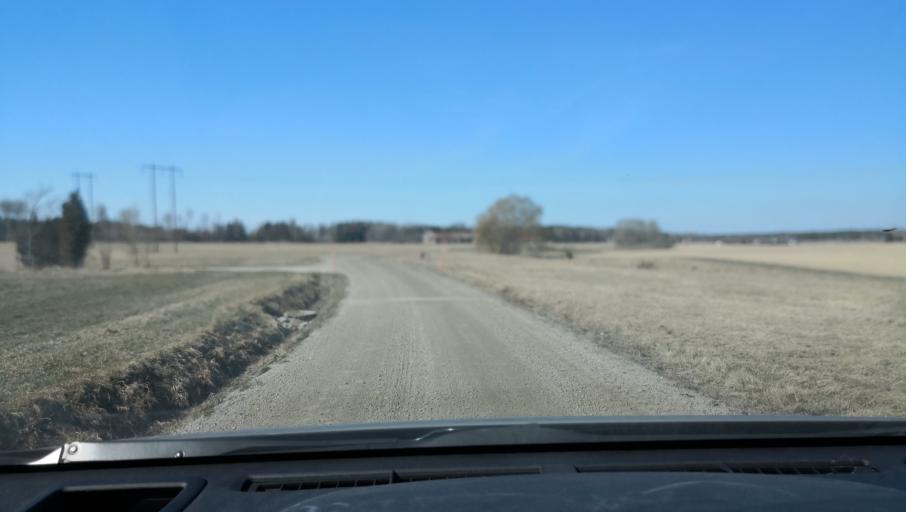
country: SE
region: Vaestmanland
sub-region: Sala Kommun
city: Sala
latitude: 59.8953
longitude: 16.5305
